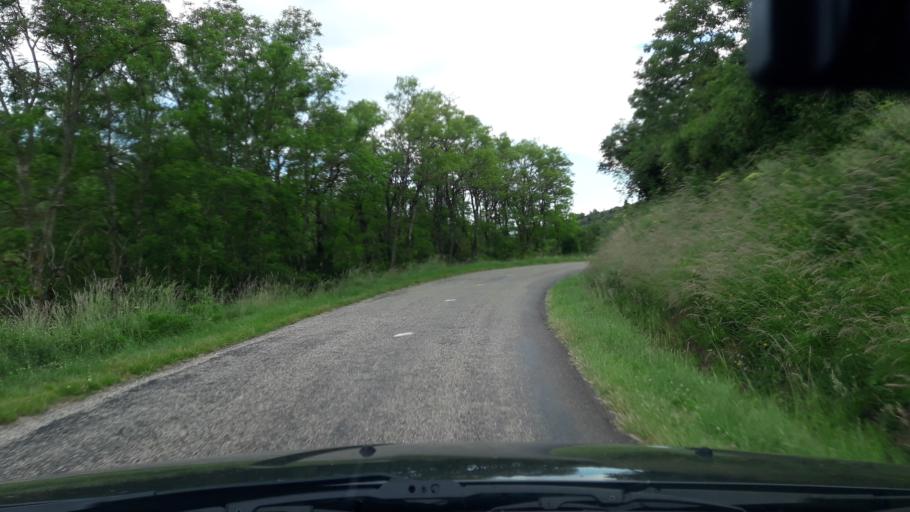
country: FR
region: Rhone-Alpes
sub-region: Departement de l'Ardeche
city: Saint-Priest
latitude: 44.6765
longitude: 4.5367
